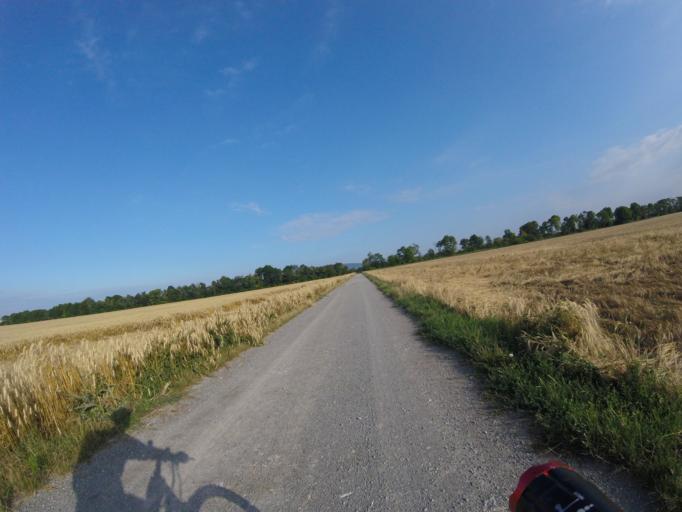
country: AT
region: Lower Austria
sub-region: Politischer Bezirk Baden
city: Trumau
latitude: 48.0004
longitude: 16.3711
